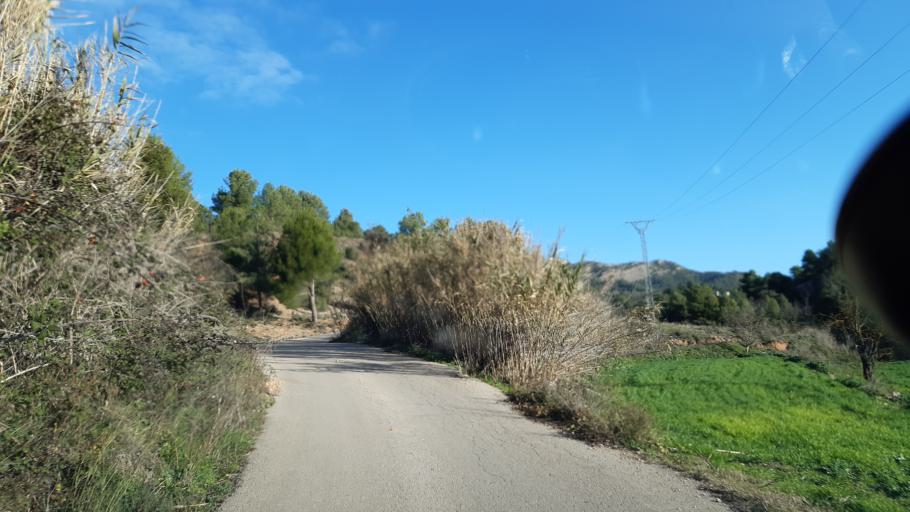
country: ES
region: Aragon
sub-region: Provincia de Teruel
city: Valderrobres
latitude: 40.8456
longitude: 0.2070
